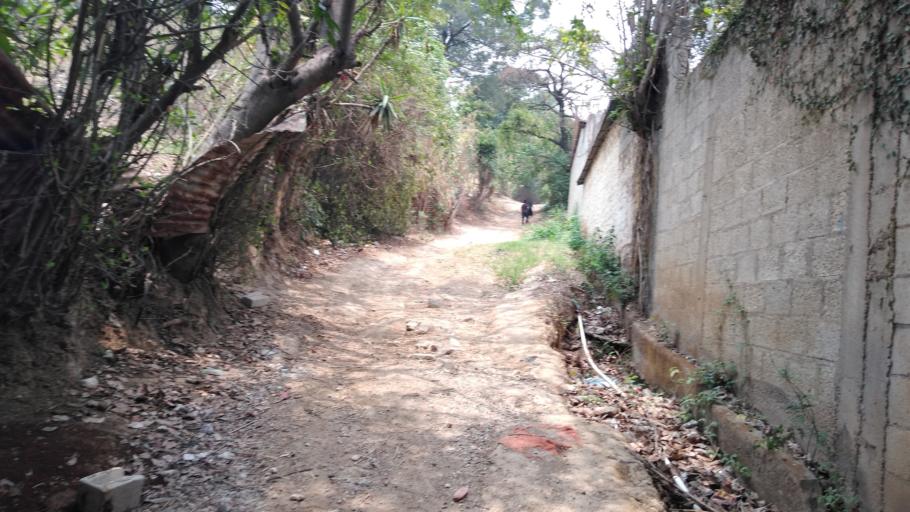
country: GT
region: Guatemala
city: Petapa
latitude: 14.5062
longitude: -90.5554
